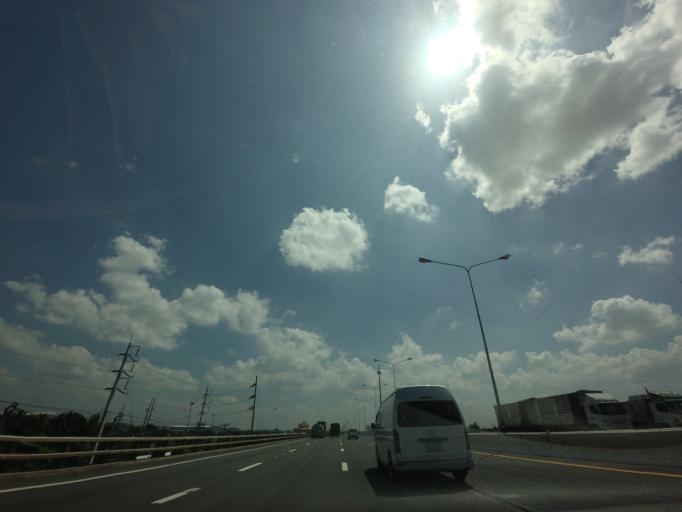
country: TH
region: Bangkok
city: Lat Krabang
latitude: 13.7116
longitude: 100.8195
